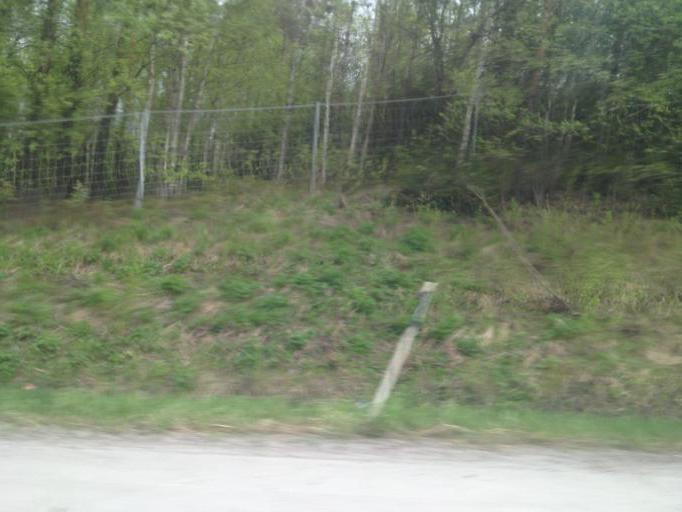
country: FI
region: Uusimaa
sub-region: Helsinki
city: Hyvinge
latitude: 60.5909
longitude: 24.7979
